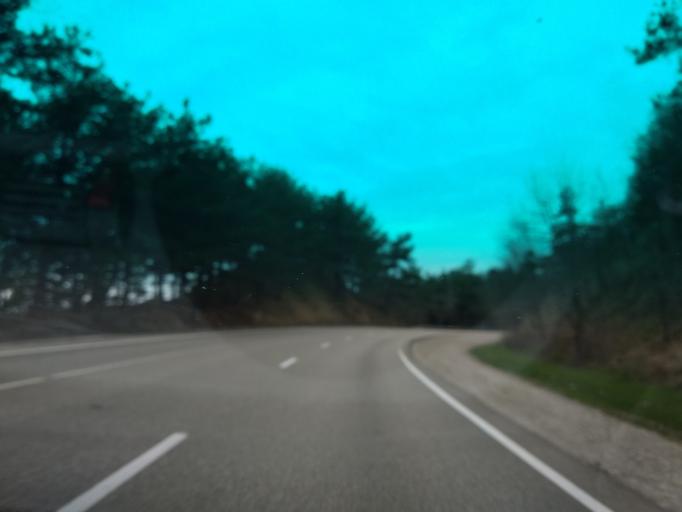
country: RU
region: Krasnodarskiy
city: Ol'ginka
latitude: 44.1862
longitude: 38.9140
